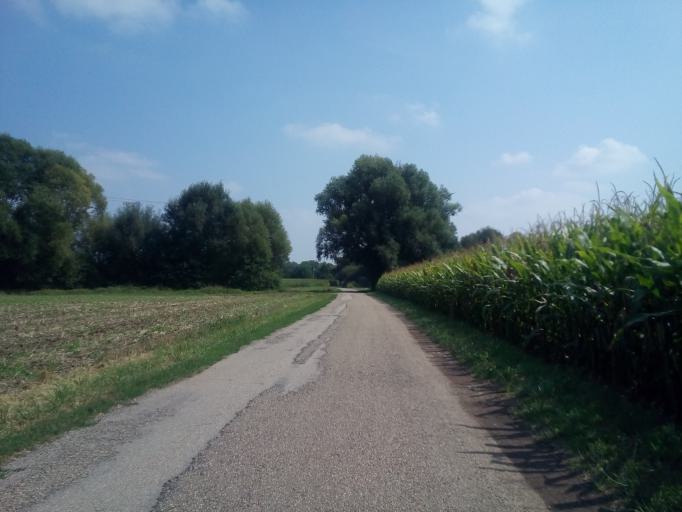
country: DE
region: Baden-Wuerttemberg
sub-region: Freiburg Region
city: Kehl
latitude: 48.6025
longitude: 7.8507
